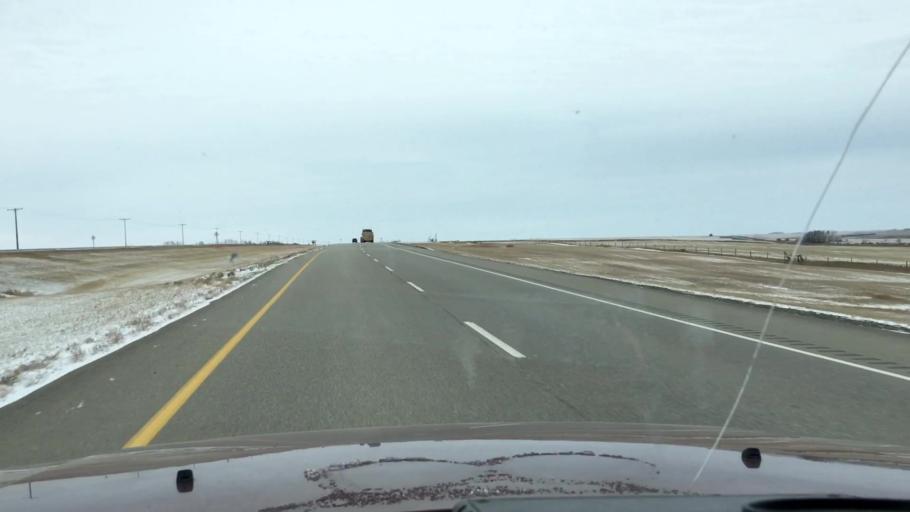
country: CA
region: Saskatchewan
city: Watrous
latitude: 51.2318
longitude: -105.9618
